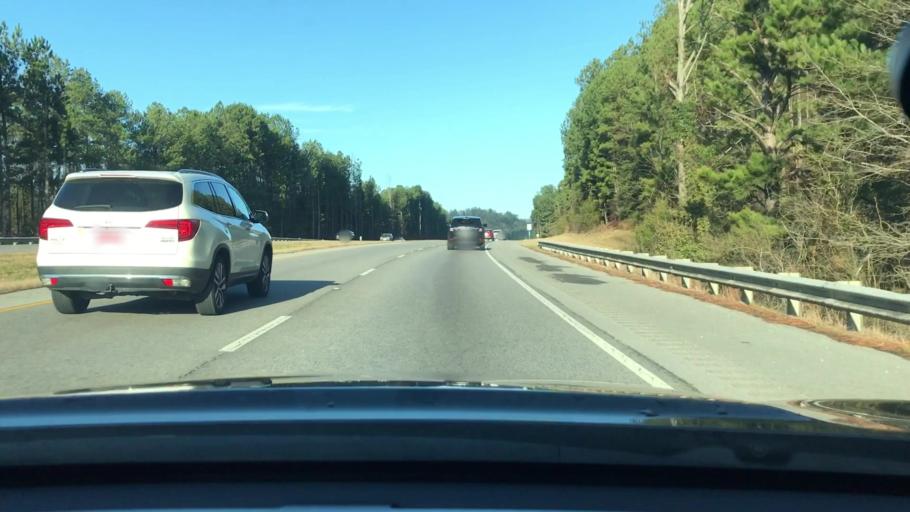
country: US
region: Alabama
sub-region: Shelby County
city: Chelsea
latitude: 33.3492
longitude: -86.6413
